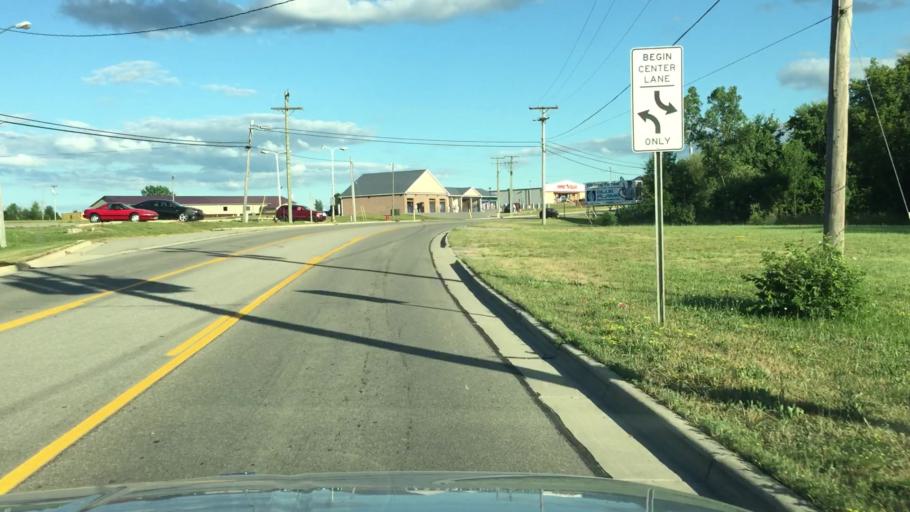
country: US
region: Michigan
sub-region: Saint Clair County
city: Yale
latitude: 43.1226
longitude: -82.7925
